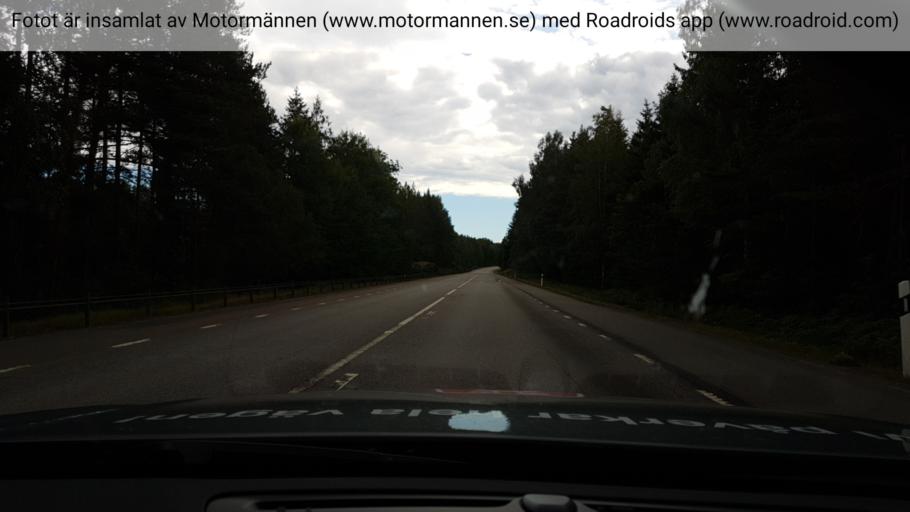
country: SE
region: Kalmar
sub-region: Vasterviks Kommun
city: Ankarsrum
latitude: 57.6233
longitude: 16.4620
